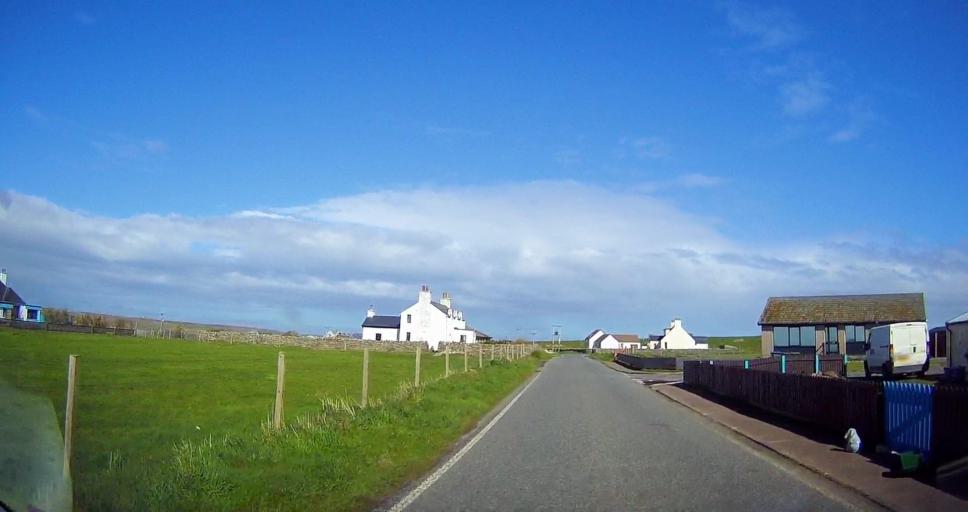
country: GB
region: Scotland
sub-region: Shetland Islands
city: Sandwick
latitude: 59.9169
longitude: -1.3152
